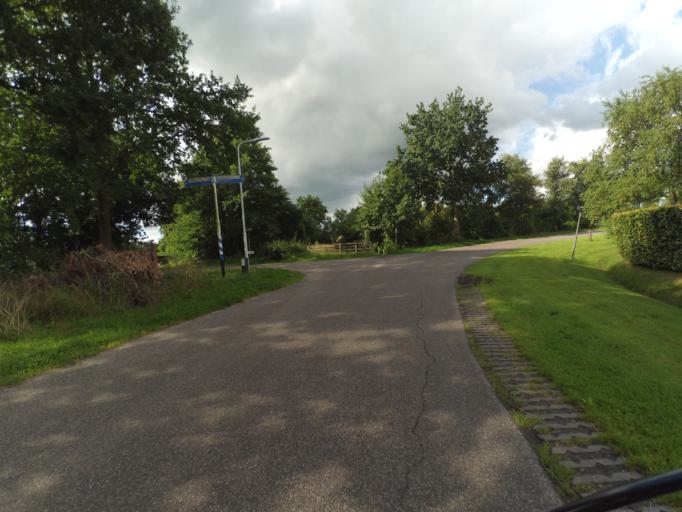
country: NL
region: Friesland
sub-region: Gemeente Tytsjerksteradiel
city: Tytsjerk
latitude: 53.2327
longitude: 5.9205
